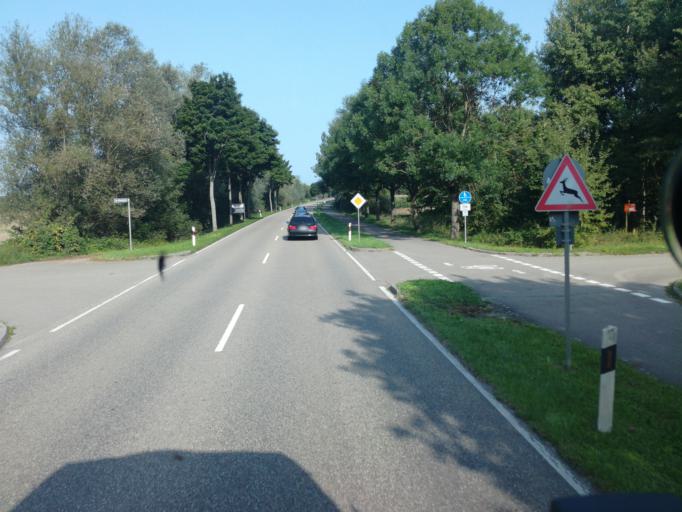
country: DE
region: Baden-Wuerttemberg
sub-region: Karlsruhe Region
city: Rastatt
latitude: 48.8494
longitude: 8.1962
